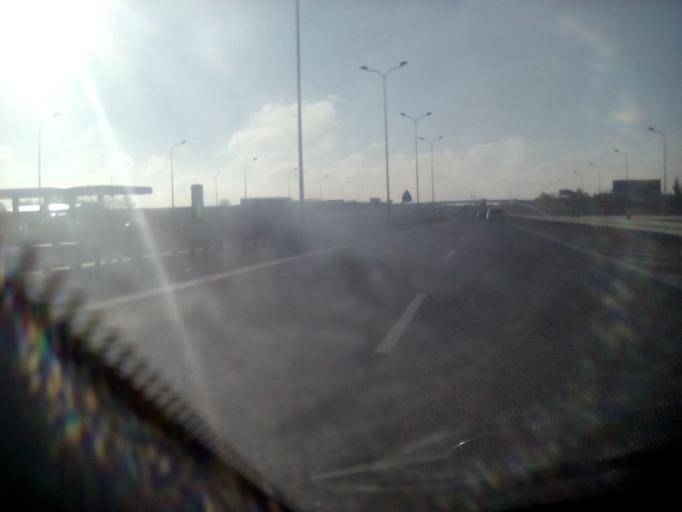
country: PL
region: Masovian Voivodeship
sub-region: Powiat grojecki
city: Grojec
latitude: 51.8354
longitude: 20.8769
